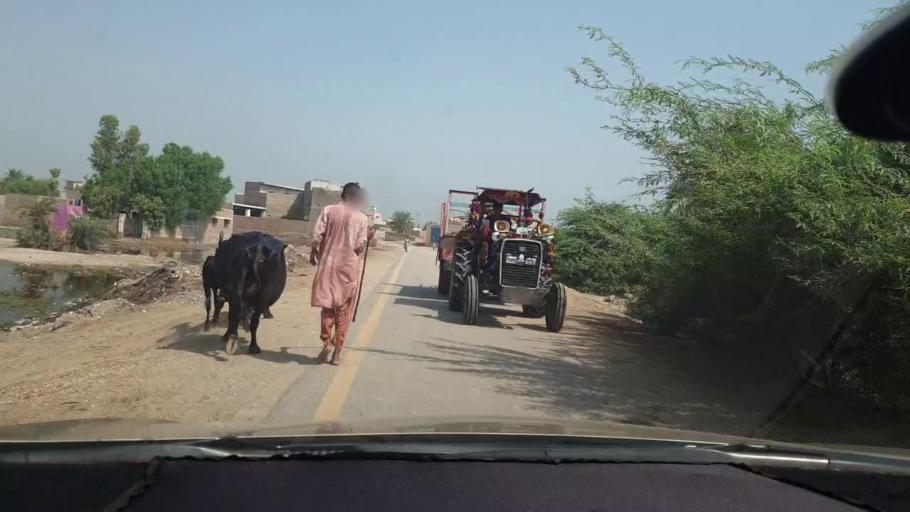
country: PK
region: Sindh
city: Kambar
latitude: 27.5802
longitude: 68.0064
